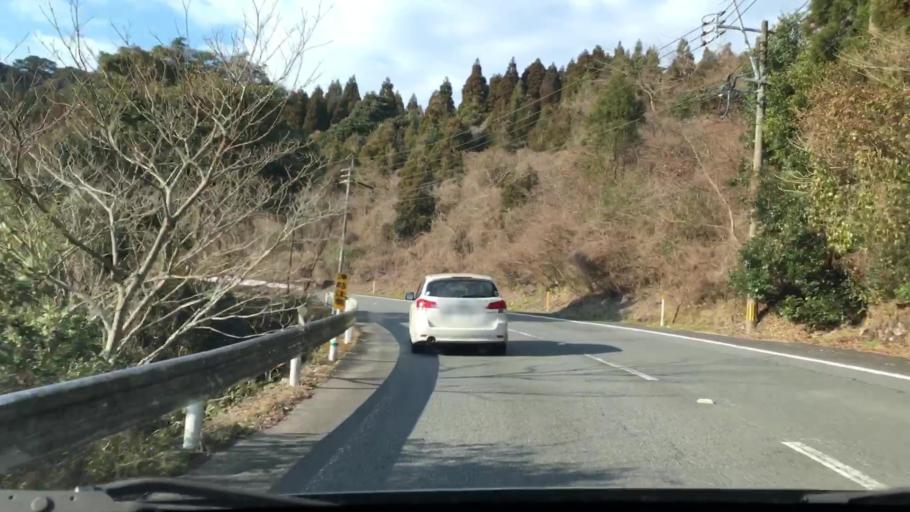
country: JP
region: Miyazaki
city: Miyazaki-shi
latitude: 31.7790
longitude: 131.3301
